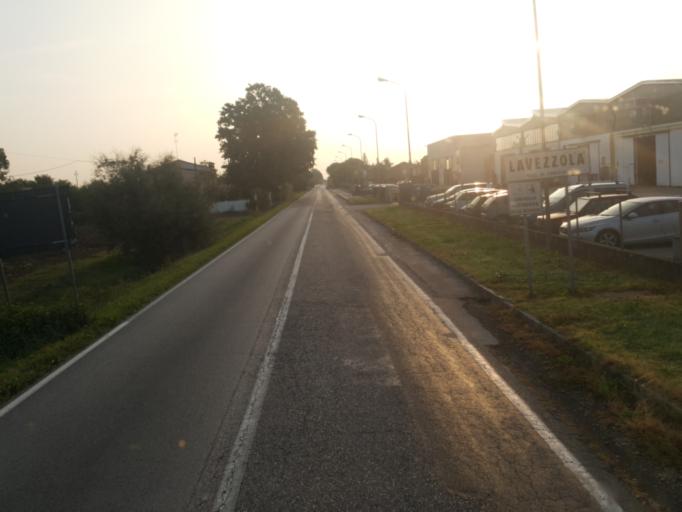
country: IT
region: Emilia-Romagna
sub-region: Provincia di Ravenna
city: Lavezzola
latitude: 44.5573
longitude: 11.8619
